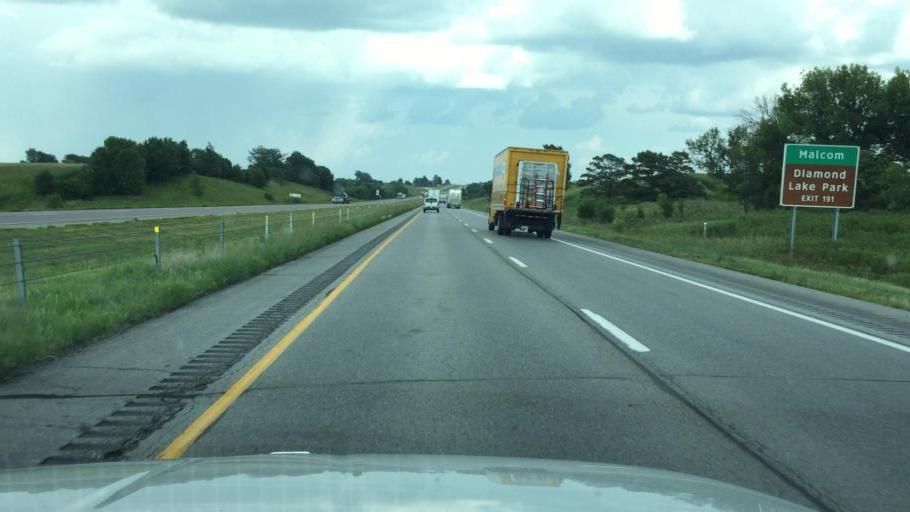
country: US
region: Iowa
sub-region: Poweshiek County
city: Montezuma
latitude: 41.6961
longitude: -92.5720
